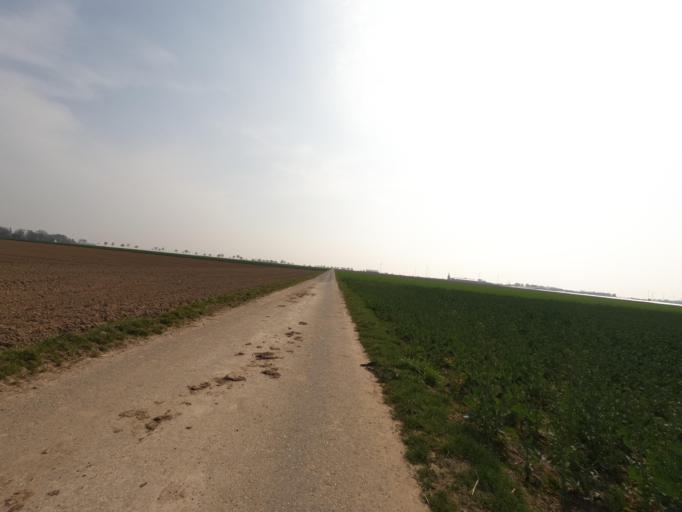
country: DE
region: North Rhine-Westphalia
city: Erkelenz
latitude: 51.0464
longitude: 6.3600
